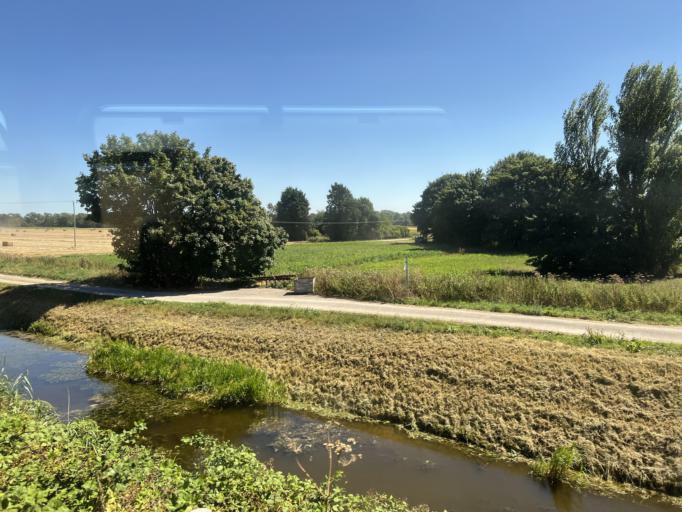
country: GB
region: England
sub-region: Lincolnshire
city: Spilsby
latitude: 53.1110
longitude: 0.1244
